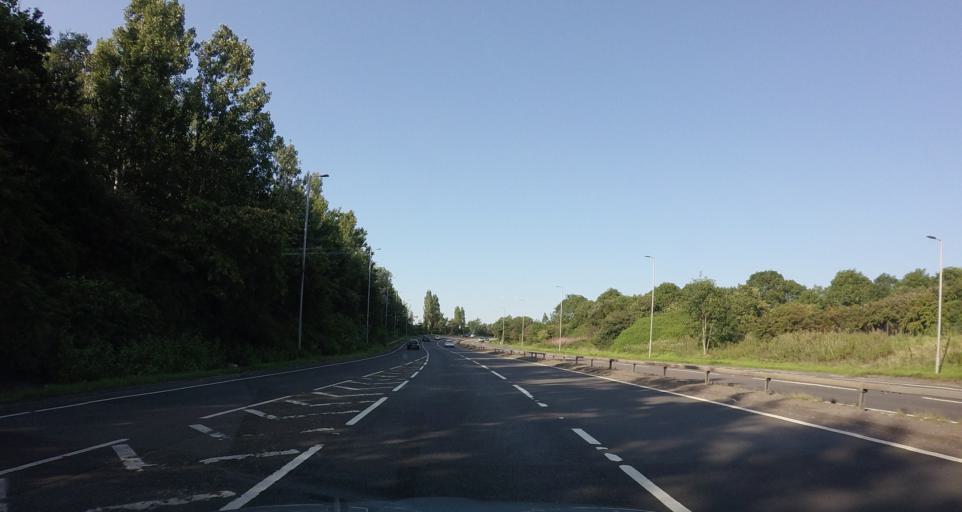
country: GB
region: Scotland
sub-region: South Lanarkshire
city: High Blantyre
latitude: 55.7864
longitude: -4.0867
